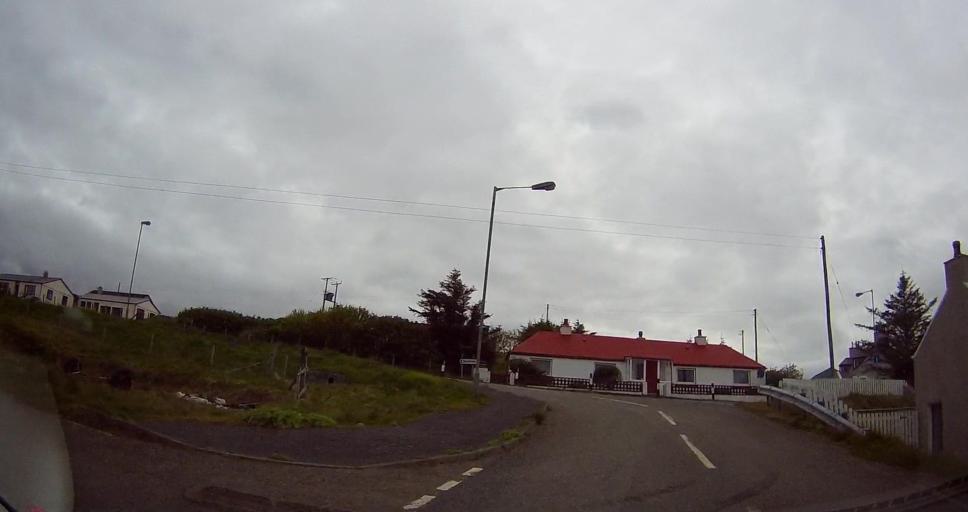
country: GB
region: Scotland
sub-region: Shetland Islands
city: Shetland
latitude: 60.5987
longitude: -1.0740
